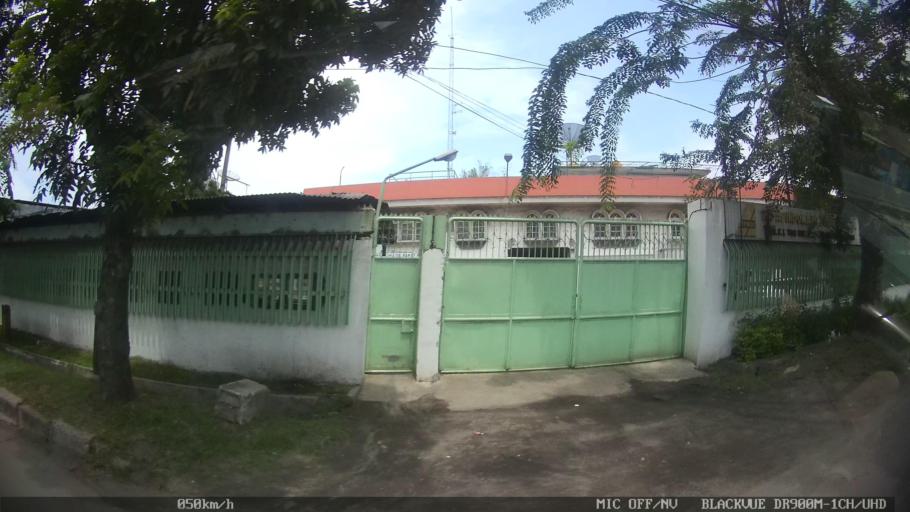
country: ID
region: North Sumatra
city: Labuhan Deli
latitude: 3.6720
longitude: 98.6667
